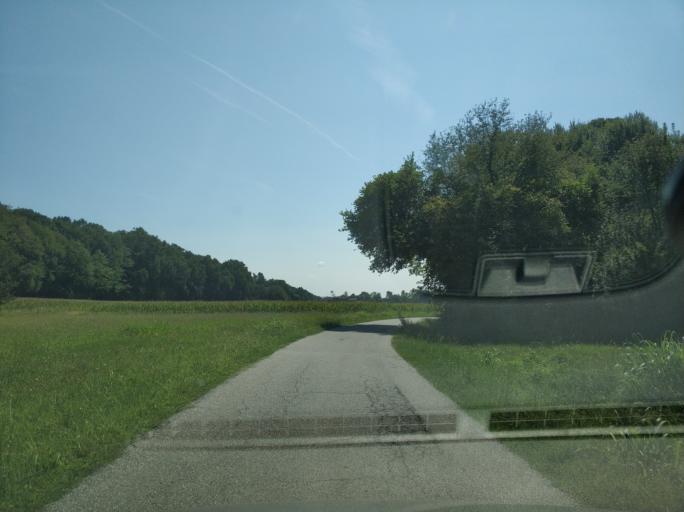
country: IT
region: Piedmont
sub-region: Provincia di Torino
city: San Carlo Canavese
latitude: 45.2355
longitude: 7.6227
